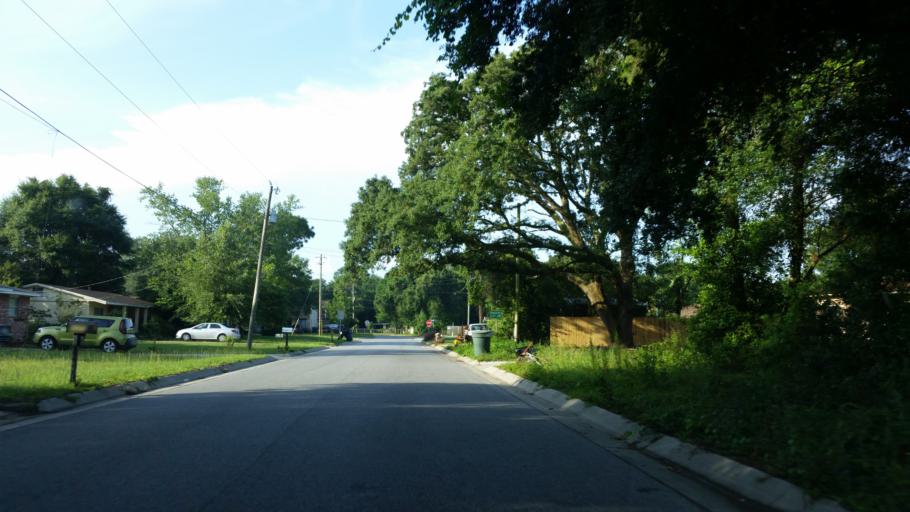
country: US
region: Florida
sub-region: Escambia County
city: Ferry Pass
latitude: 30.4892
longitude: -87.2010
